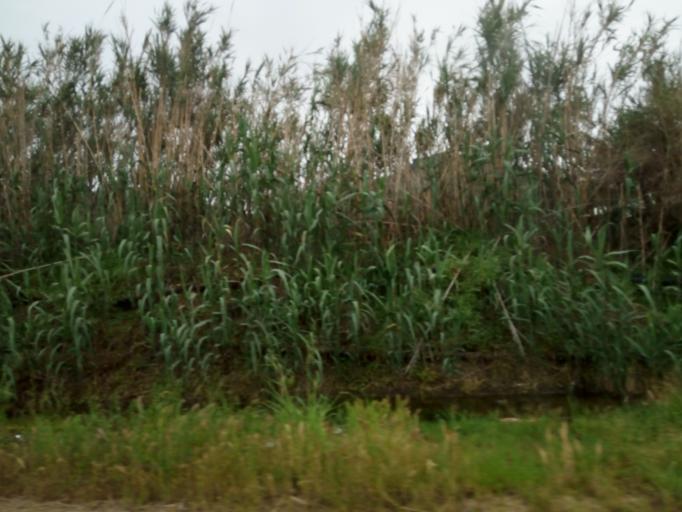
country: DZ
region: Tipaza
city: Tipasa
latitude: 36.5896
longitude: 2.5428
